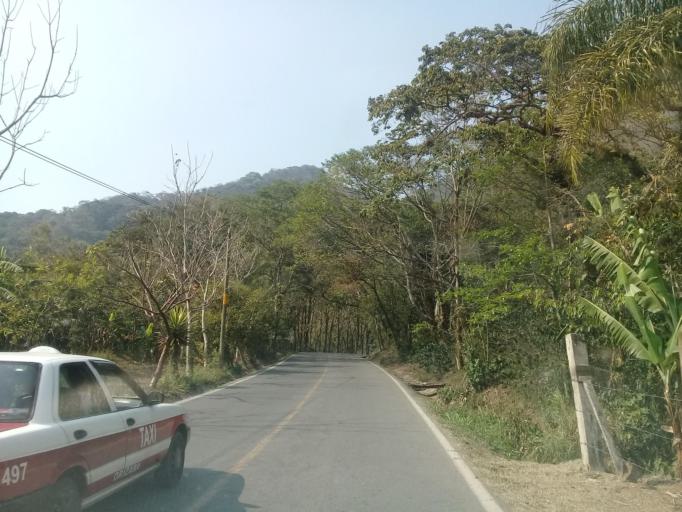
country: MX
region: Veracruz
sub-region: Ixtaczoquitlan
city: Campo Chico
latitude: 18.8382
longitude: -97.0230
